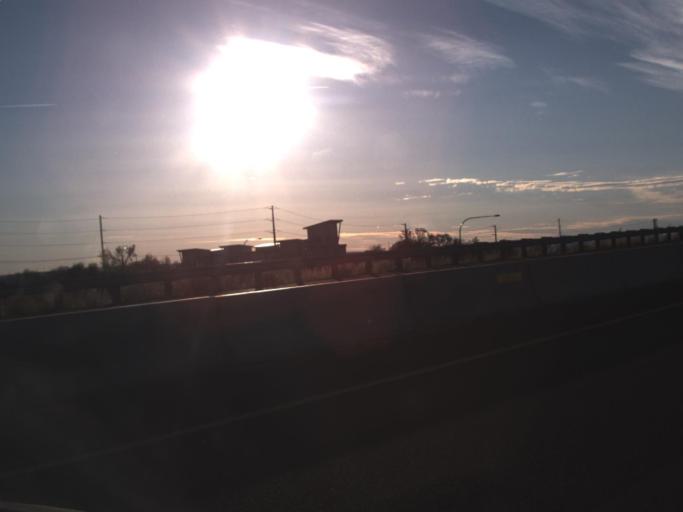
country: US
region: Washington
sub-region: Walla Walla County
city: Walla Walla
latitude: 46.0697
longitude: -118.3684
